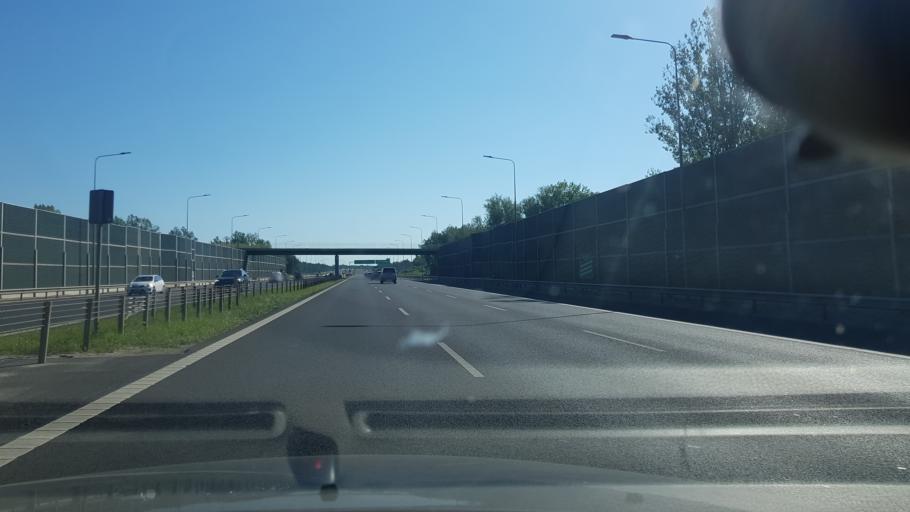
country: PL
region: Masovian Voivodeship
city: Zielonka
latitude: 52.3162
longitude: 21.1338
